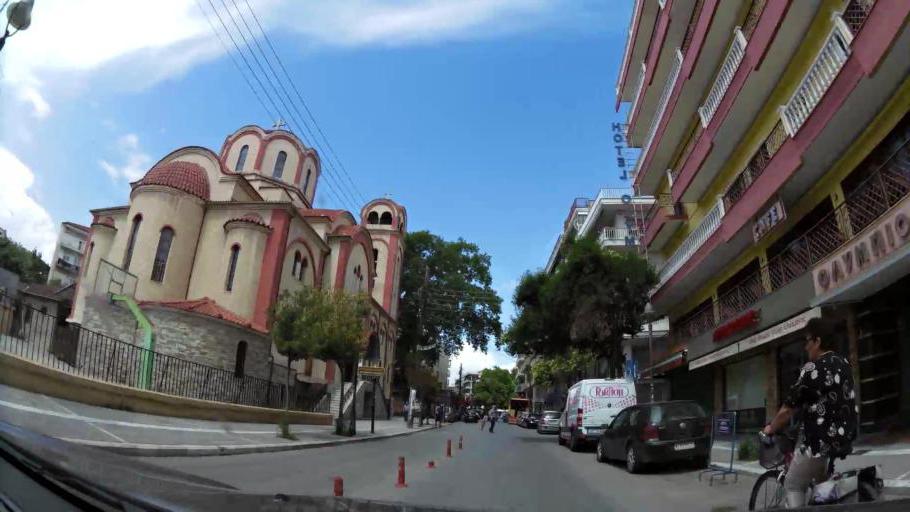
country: GR
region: Central Macedonia
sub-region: Nomos Pierias
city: Katerini
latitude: 40.2707
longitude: 22.5107
